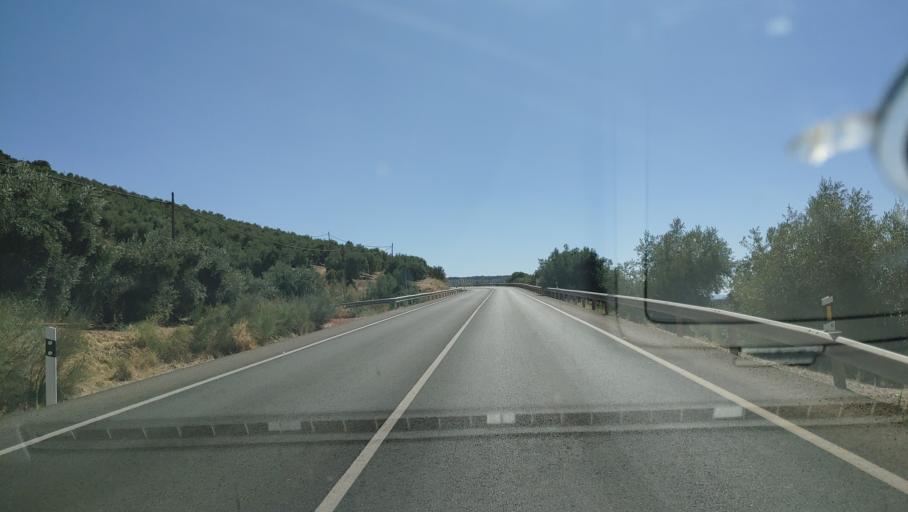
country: ES
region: Andalusia
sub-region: Provincia de Jaen
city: Campina
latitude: 38.2497
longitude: -2.9633
